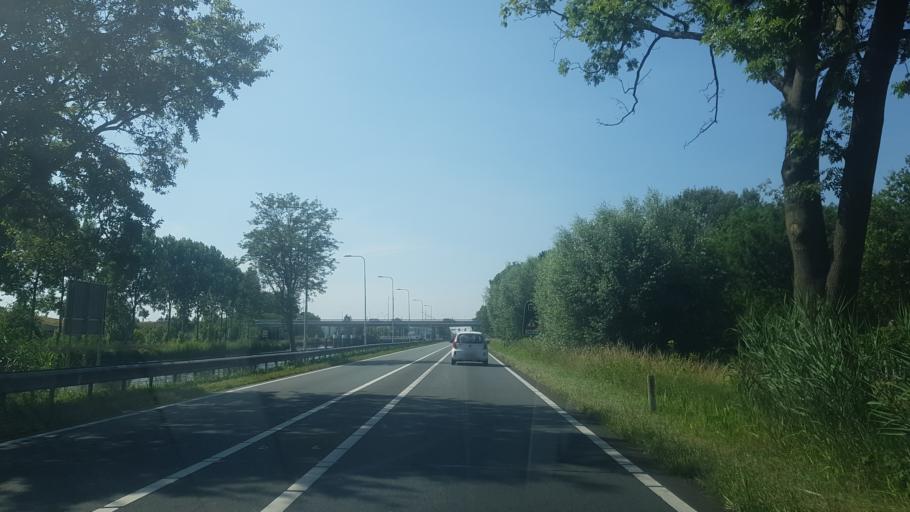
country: NL
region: North Brabant
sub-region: Gemeente Veghel
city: Zijtaart
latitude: 51.6068
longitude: 5.5354
